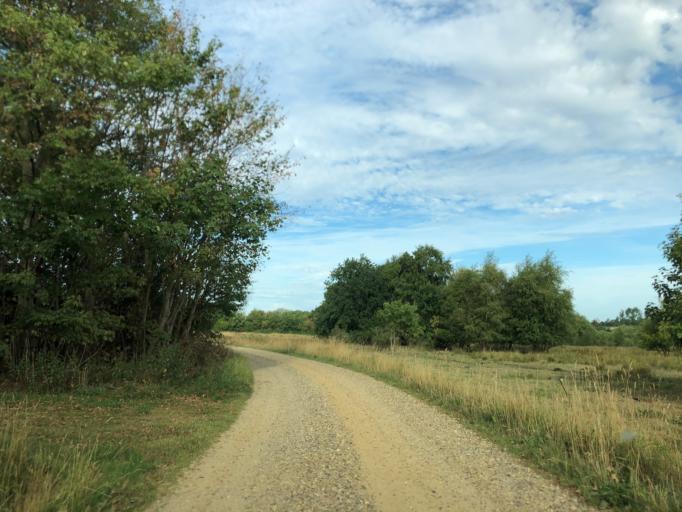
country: DK
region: Central Jutland
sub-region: Ringkobing-Skjern Kommune
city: Skjern
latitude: 56.0412
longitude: 8.4270
